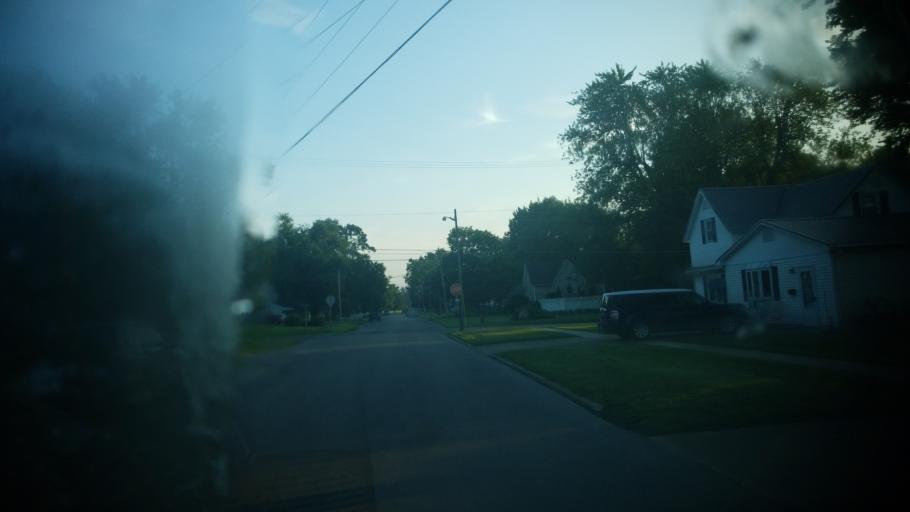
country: US
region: Illinois
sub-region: Wayne County
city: Fairfield
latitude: 38.3833
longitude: -88.3718
